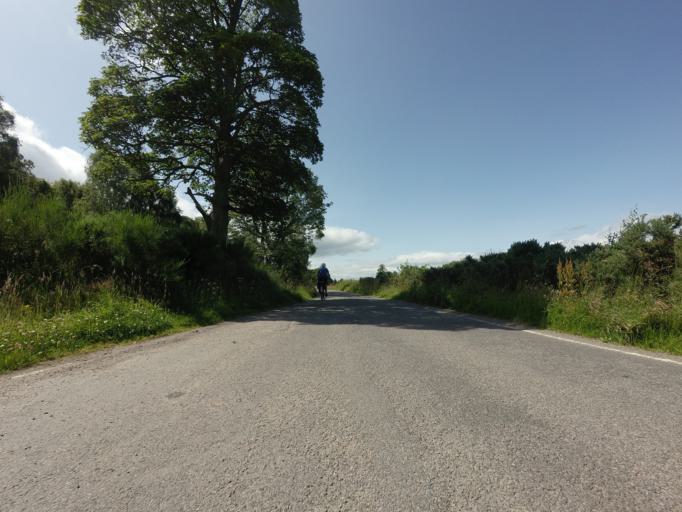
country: GB
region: Scotland
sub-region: Highland
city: Nairn
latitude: 57.5044
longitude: -3.9936
